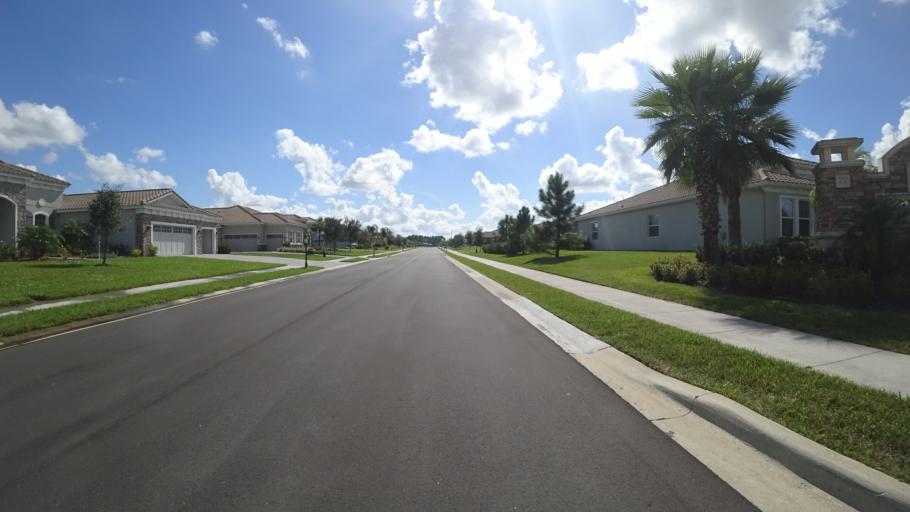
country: US
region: Florida
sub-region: Manatee County
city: Ellenton
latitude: 27.4973
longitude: -82.3690
